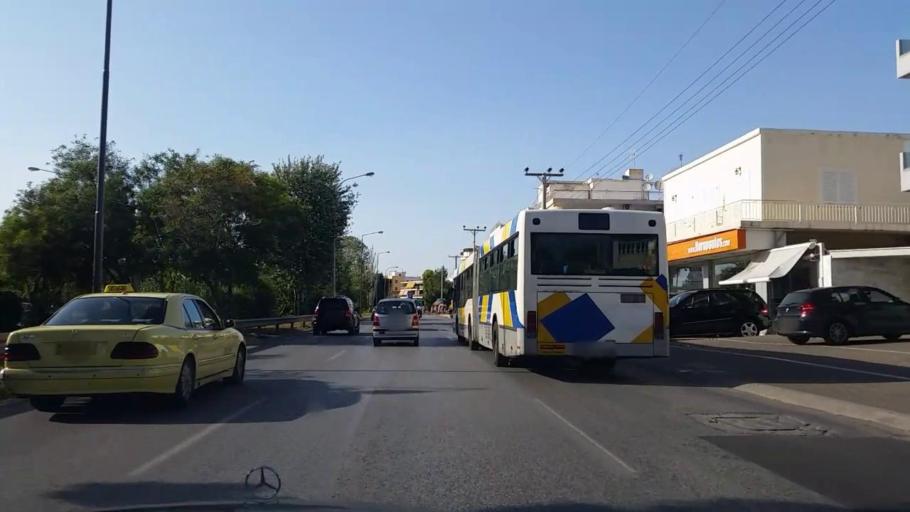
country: GR
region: Attica
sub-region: Nomarchia Athinas
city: Glyfada
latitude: 37.8495
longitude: 23.7531
